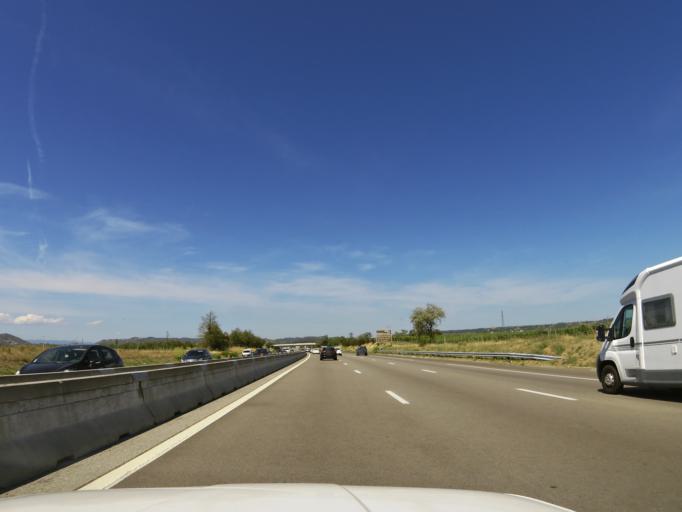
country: FR
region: Rhone-Alpes
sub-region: Departement de la Drome
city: Mercurol
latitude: 45.0443
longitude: 4.8784
